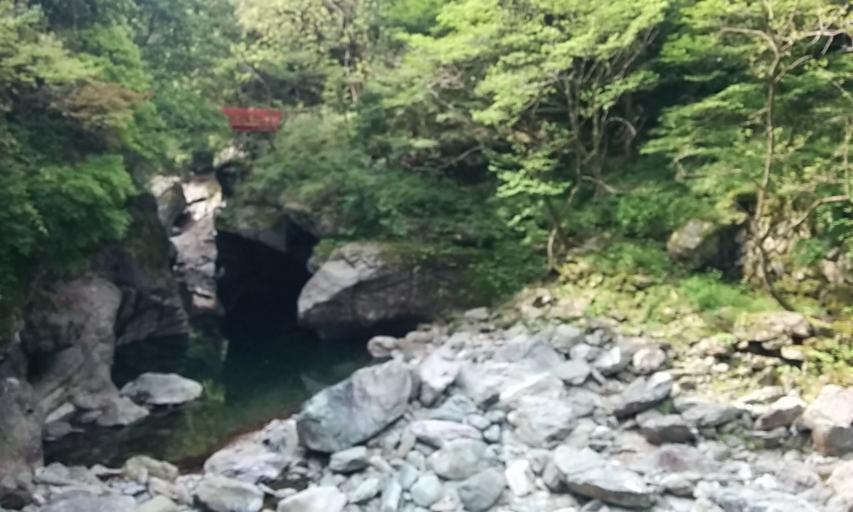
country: JP
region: Ehime
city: Niihama
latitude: 33.8985
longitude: 133.3079
